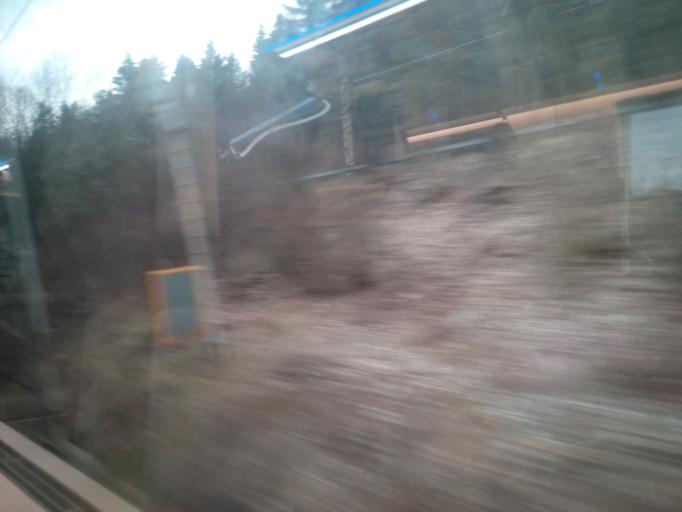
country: SK
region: Zilinsky
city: Ruzomberok
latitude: 49.0857
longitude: 19.2895
